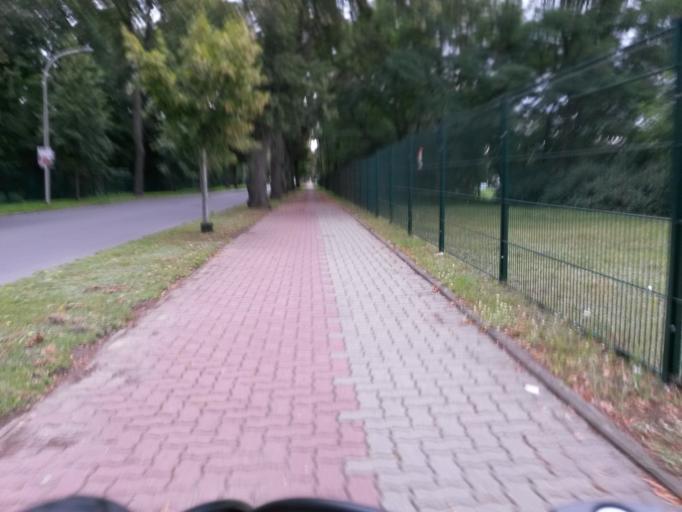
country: DE
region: Brandenburg
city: Angermunde
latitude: 53.0040
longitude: 13.9893
